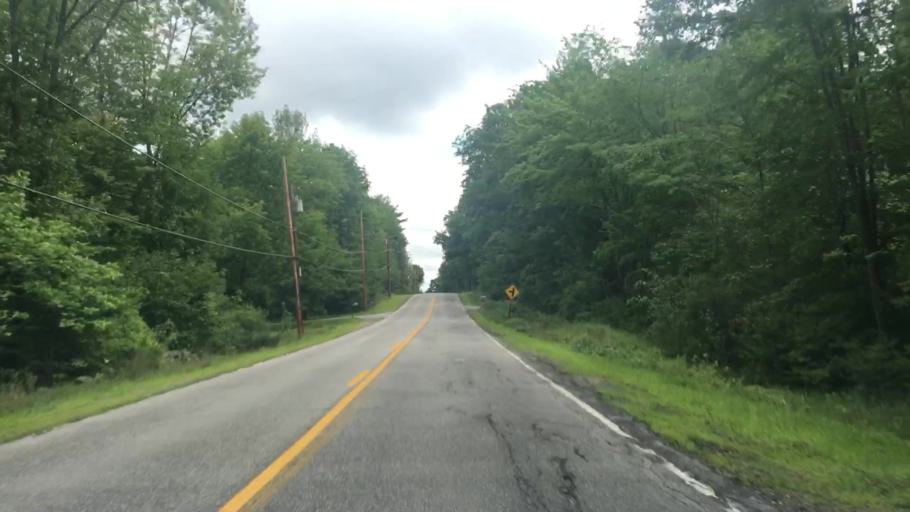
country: US
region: Maine
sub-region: York County
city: Limerick
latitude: 43.6699
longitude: -70.7754
